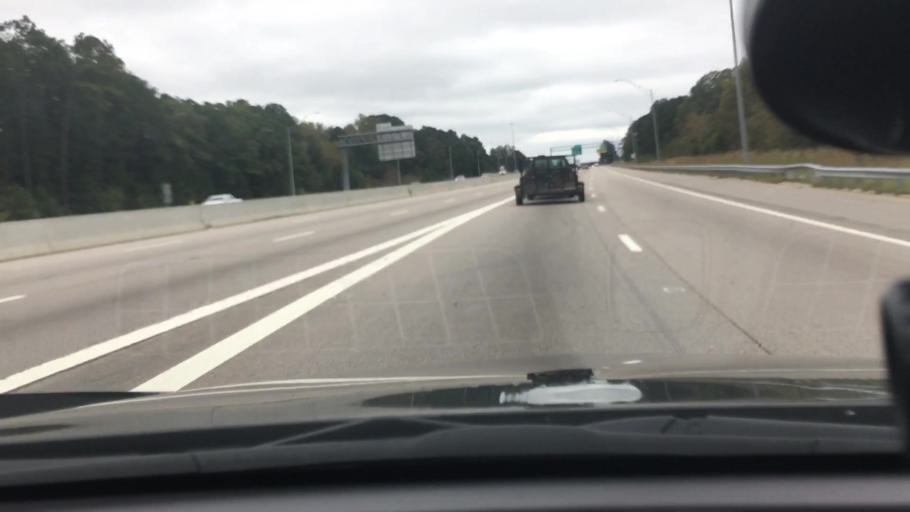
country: US
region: North Carolina
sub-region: Wake County
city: Raleigh
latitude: 35.7754
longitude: -78.5739
